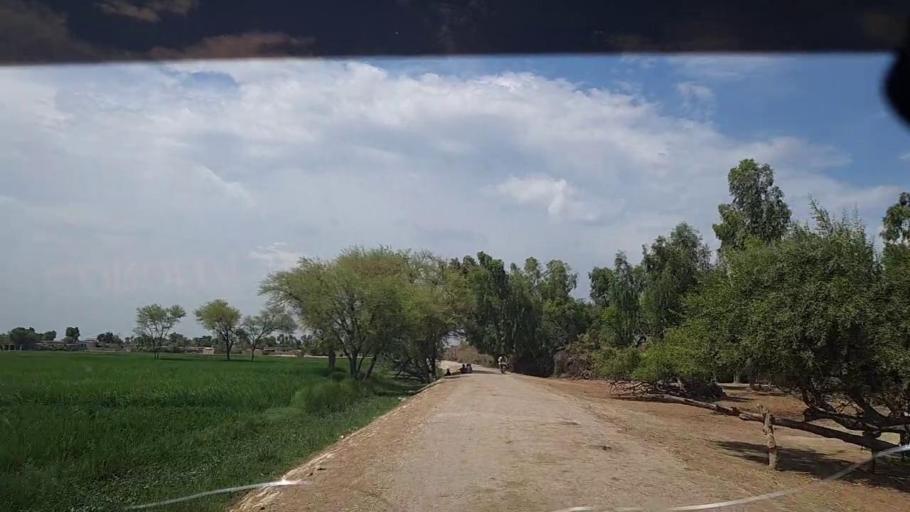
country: PK
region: Sindh
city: Ghauspur
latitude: 28.1517
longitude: 68.9975
